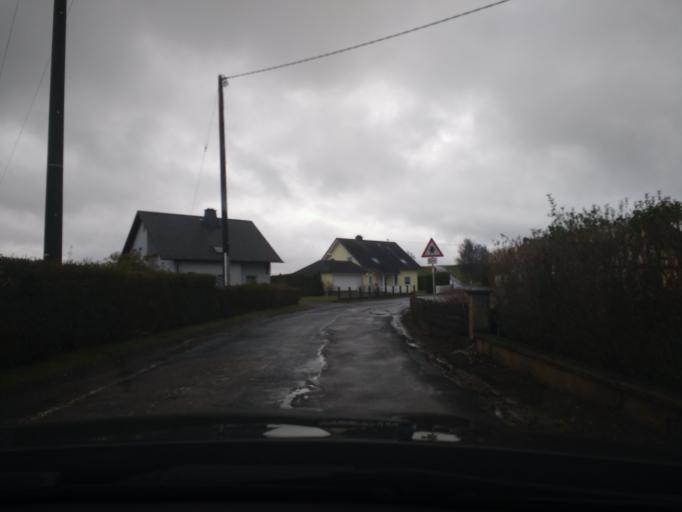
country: DE
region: Rheinland-Pfalz
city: Lampaden
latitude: 49.6594
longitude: 6.6983
